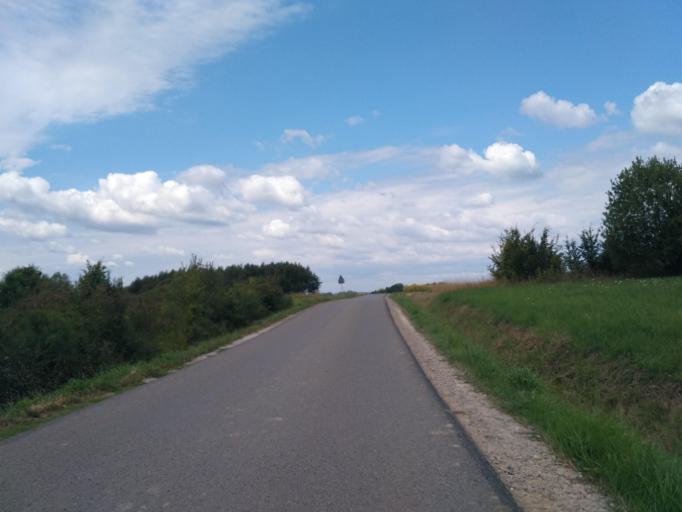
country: PL
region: Subcarpathian Voivodeship
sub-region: Powiat rzeszowski
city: Hyzne
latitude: 49.9090
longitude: 22.2229
